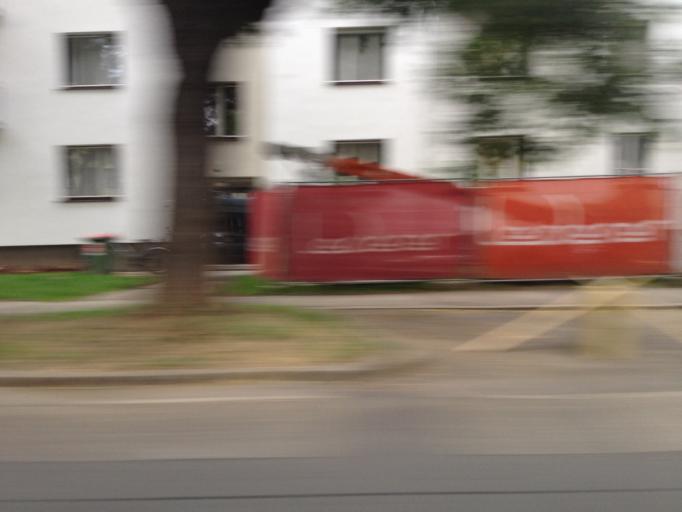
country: AT
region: Styria
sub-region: Graz Stadt
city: Graz
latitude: 47.0861
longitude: 15.4305
